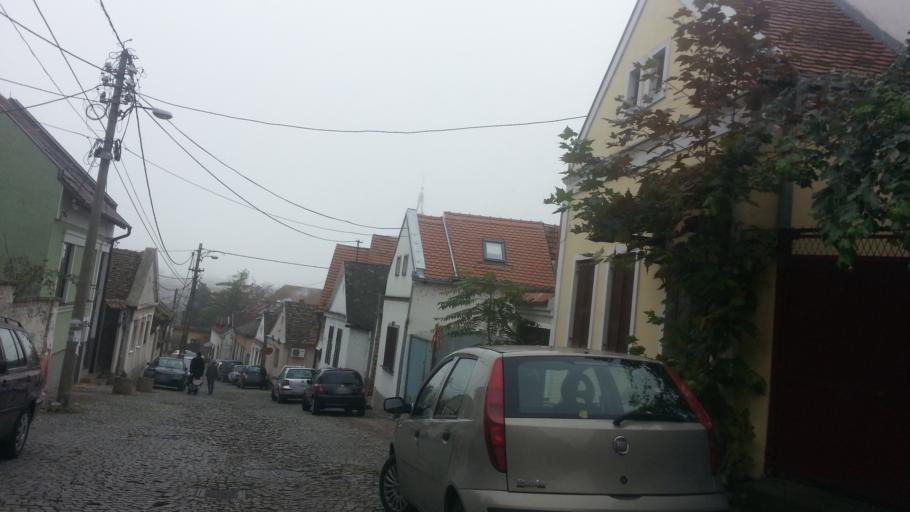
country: RS
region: Central Serbia
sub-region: Belgrade
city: Zemun
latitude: 44.8487
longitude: 20.4109
